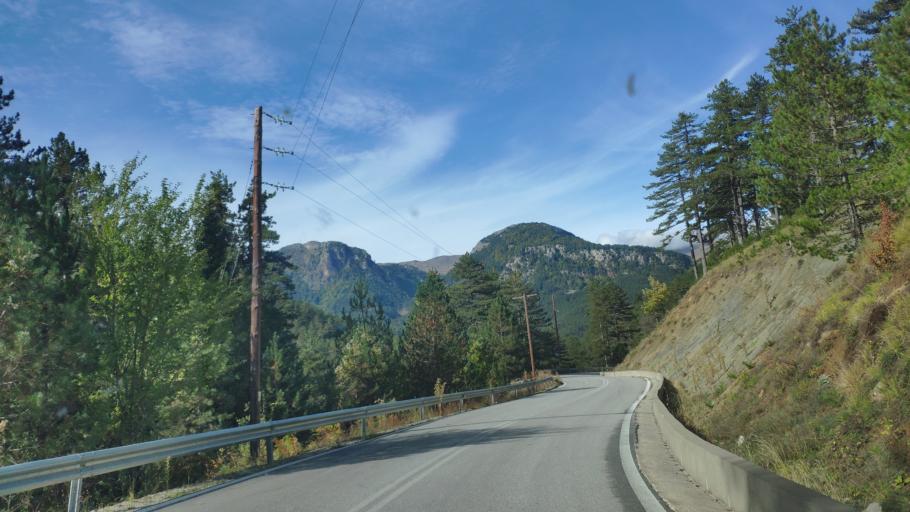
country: AL
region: Korce
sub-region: Rrethi i Devollit
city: Miras
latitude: 40.3988
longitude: 20.9003
